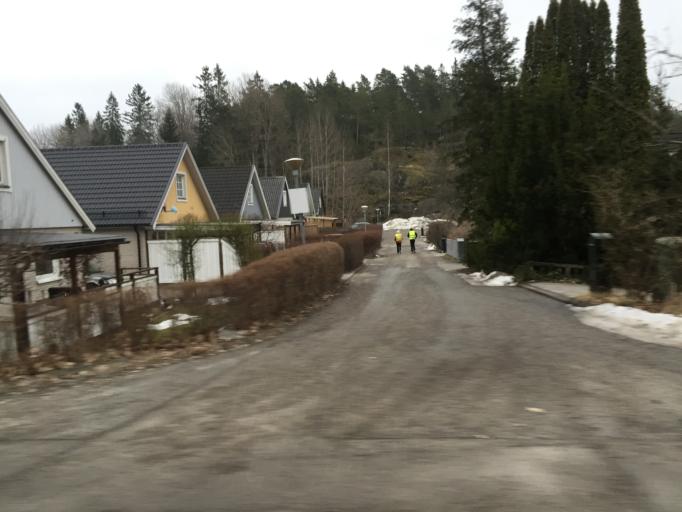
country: SE
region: Stockholm
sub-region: Salems Kommun
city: Ronninge
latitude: 59.1853
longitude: 17.7309
